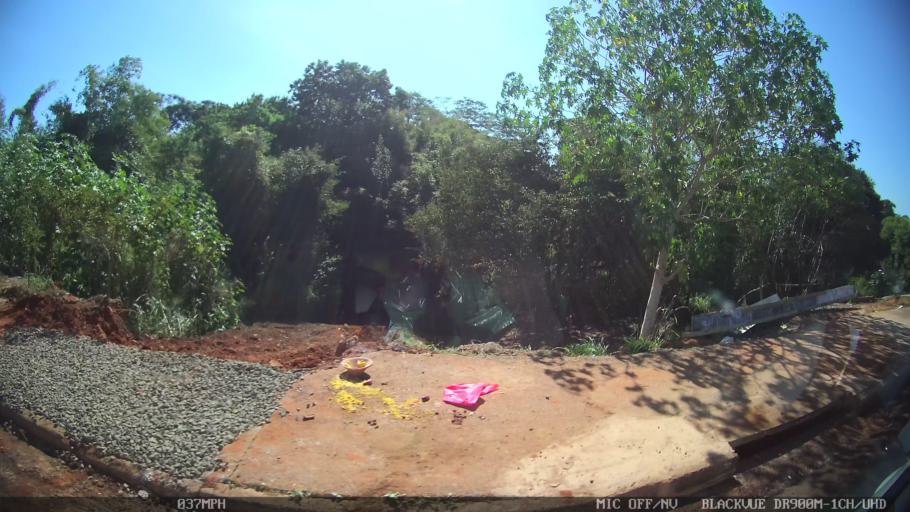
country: BR
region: Sao Paulo
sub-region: Sao Jose Do Rio Preto
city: Sao Jose do Rio Preto
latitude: -20.7783
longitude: -49.3901
